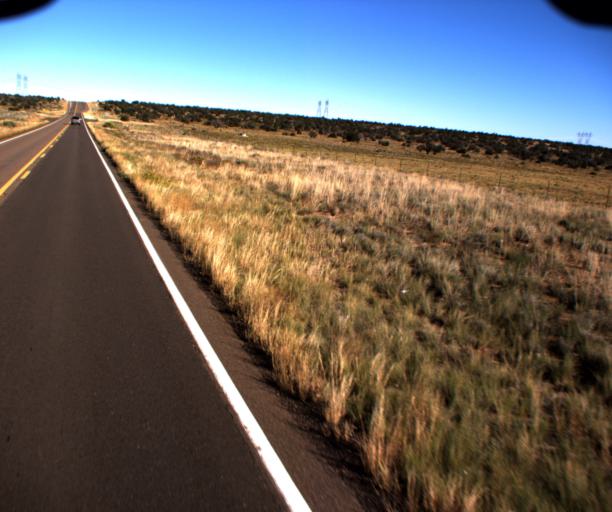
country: US
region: Arizona
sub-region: Navajo County
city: Snowflake
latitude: 34.6238
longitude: -110.0928
